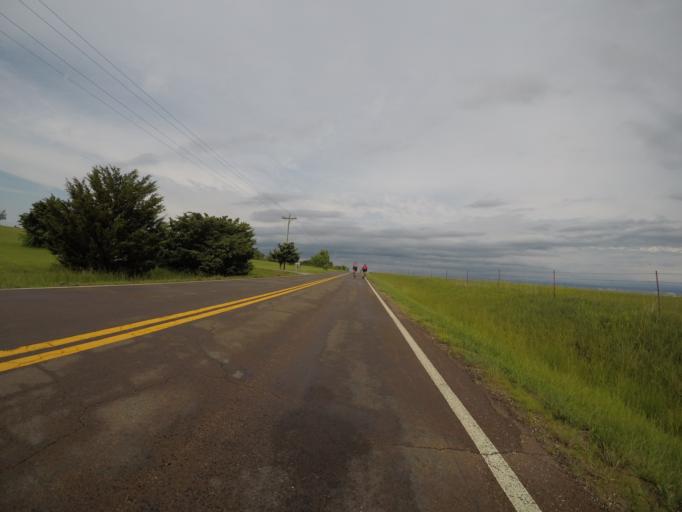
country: US
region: Kansas
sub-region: Shawnee County
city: Auburn
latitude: 38.9566
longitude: -95.8373
